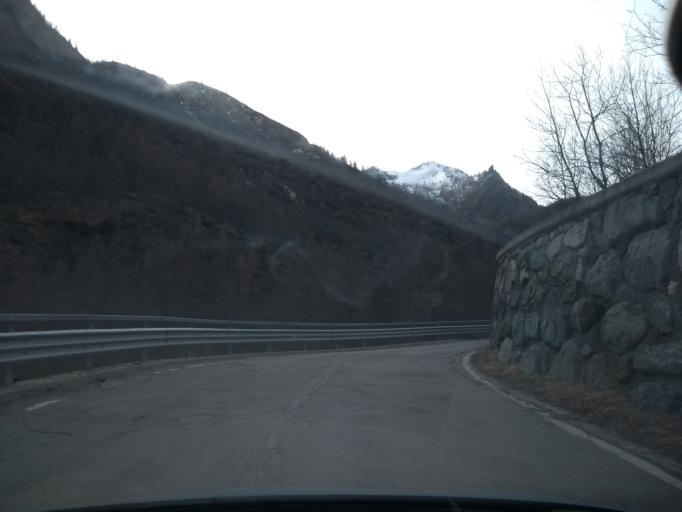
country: IT
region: Piedmont
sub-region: Provincia di Torino
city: Balme
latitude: 45.3099
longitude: 7.2492
